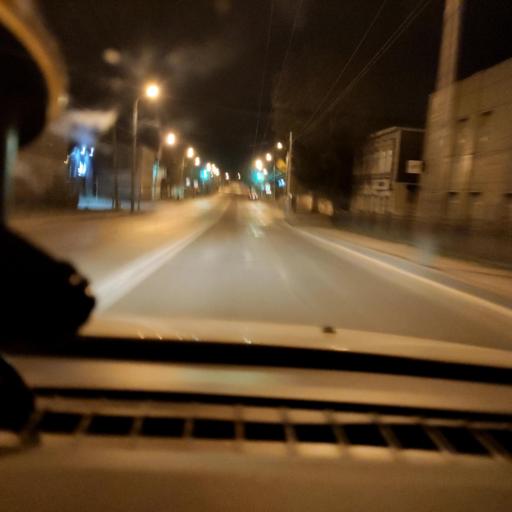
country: RU
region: Samara
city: Rozhdestveno
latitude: 53.1691
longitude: 50.0754
